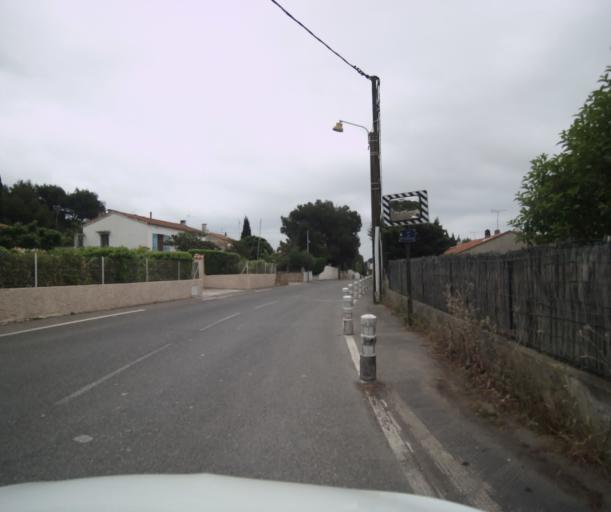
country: FR
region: Provence-Alpes-Cote d'Azur
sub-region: Departement du Var
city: Ollioules
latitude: 43.1438
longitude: 5.8846
